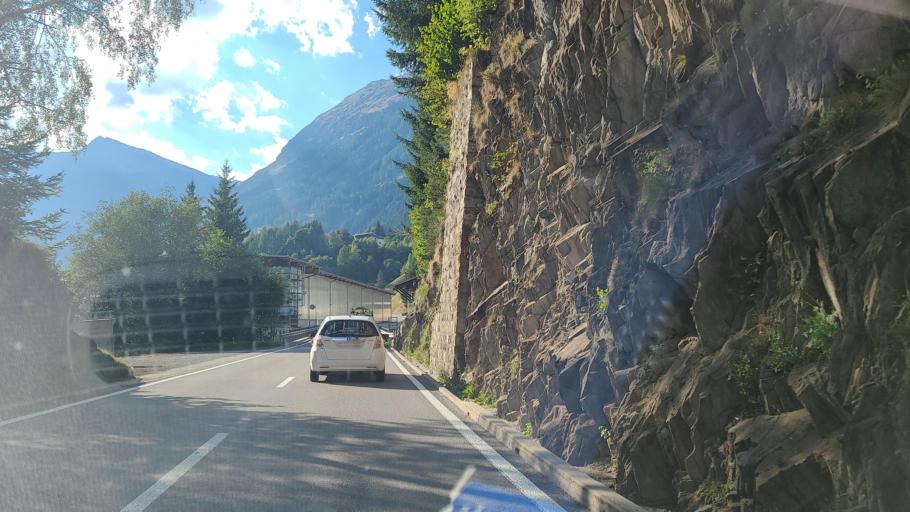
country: CH
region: Ticino
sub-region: Leventina District
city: Airolo
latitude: 46.5255
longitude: 8.6258
